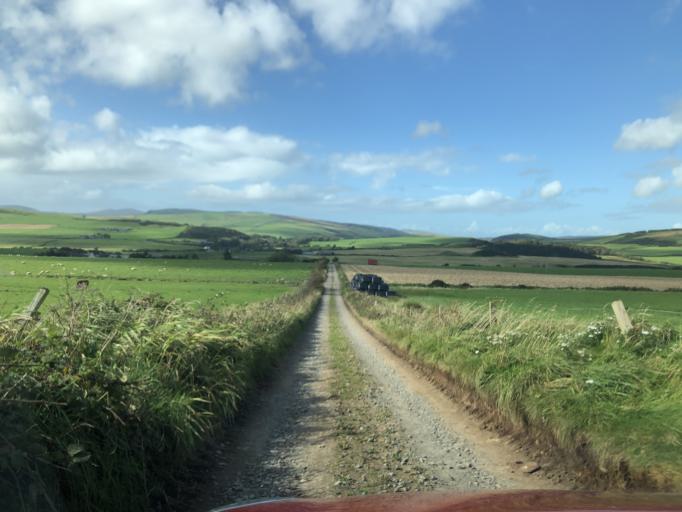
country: GB
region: Scotland
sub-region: Argyll and Bute
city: Campbeltown
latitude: 55.3161
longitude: -5.6106
